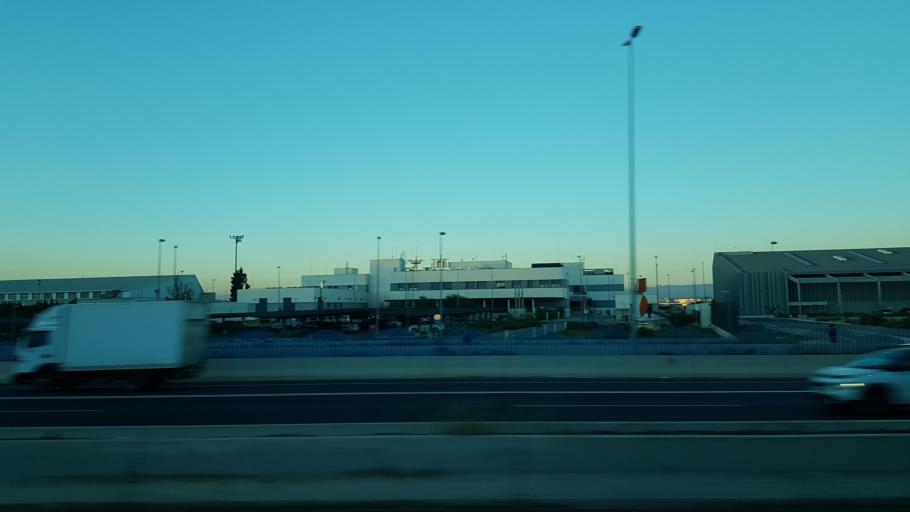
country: ES
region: Valencia
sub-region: Provincia de Valencia
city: Manises
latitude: 39.4782
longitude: -0.4749
